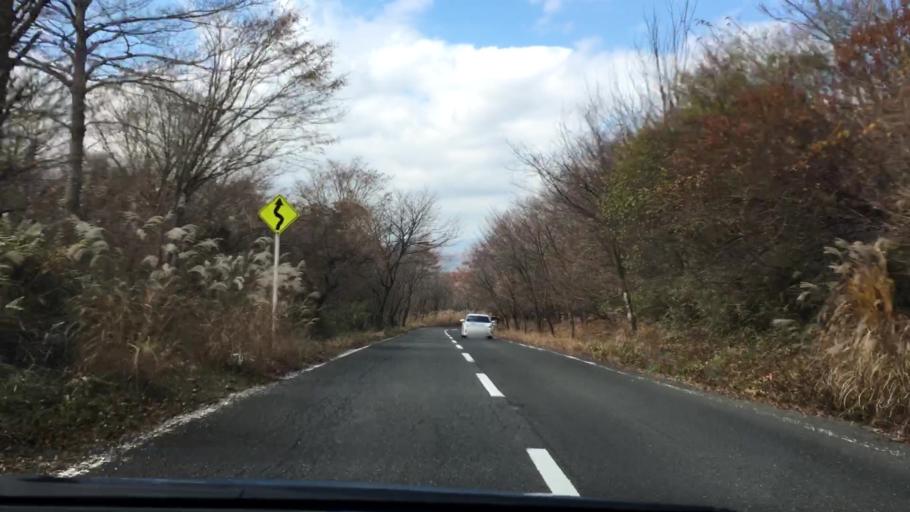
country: JP
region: Shizuoka
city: Gotemba
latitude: 35.4059
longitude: 138.9147
